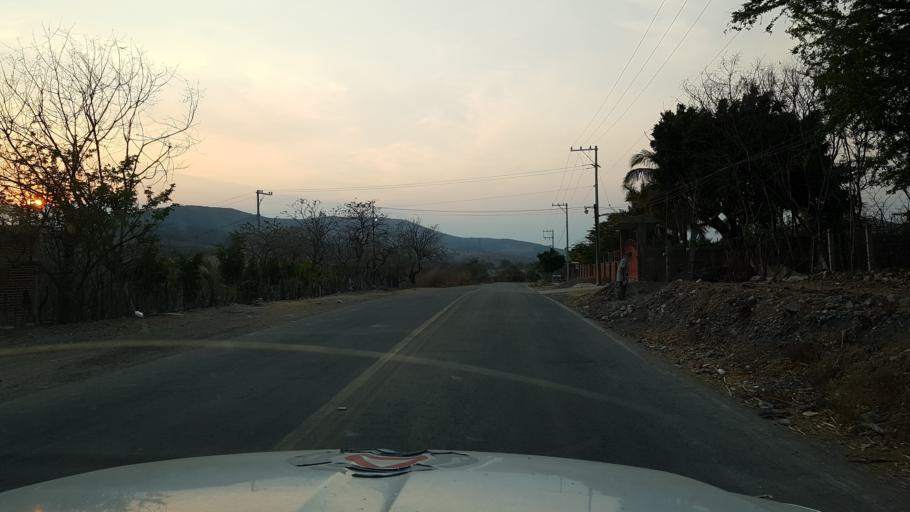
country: MX
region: Morelos
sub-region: Ayala
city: Olintepec
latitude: 18.7302
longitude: -99.0036
